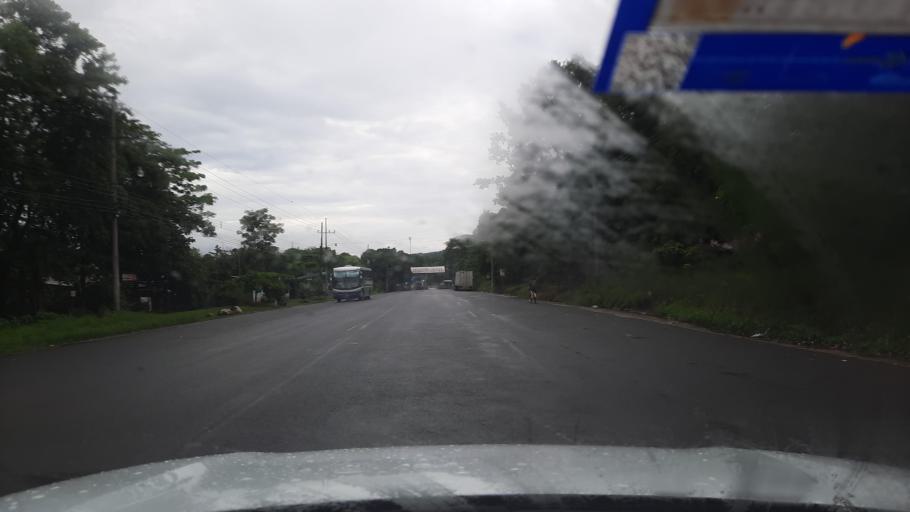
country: NI
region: Rivas
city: Cardenas
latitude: 11.2060
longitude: -85.6148
